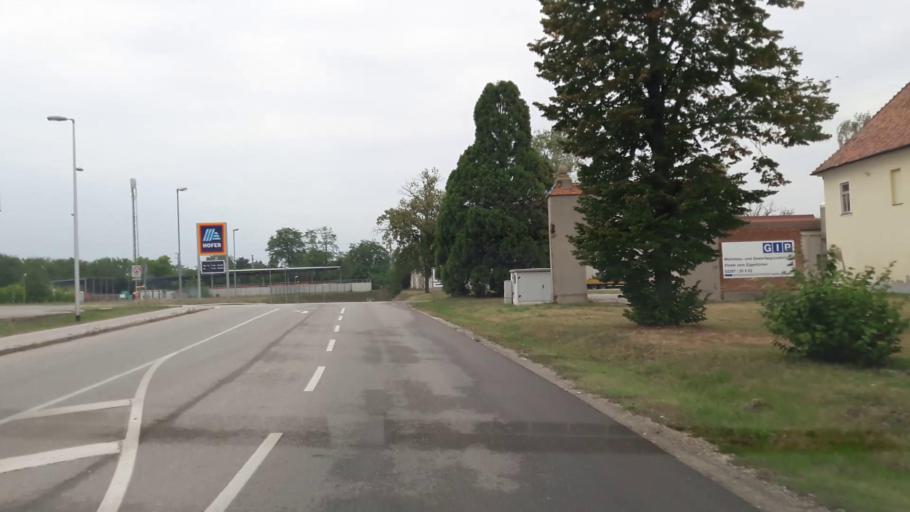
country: AT
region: Lower Austria
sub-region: Politischer Bezirk Ganserndorf
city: Strasshof an der Nordbahn
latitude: 48.3210
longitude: 16.6528
